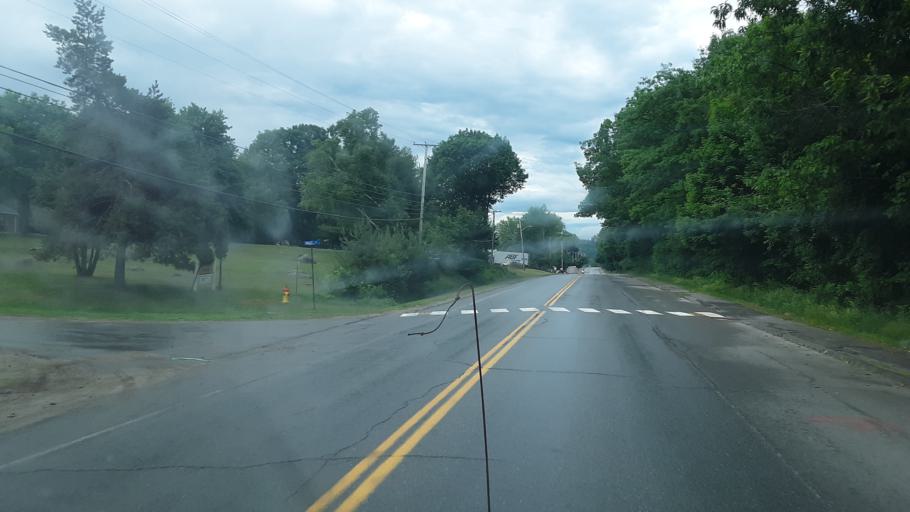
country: US
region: Maine
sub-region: Penobscot County
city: Lincoln
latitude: 45.3755
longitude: -68.5013
